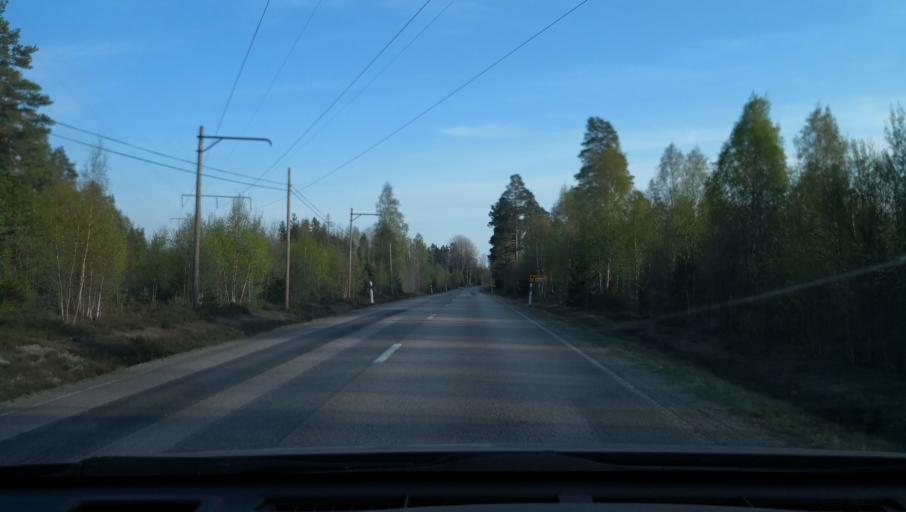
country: SE
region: Uppsala
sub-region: Heby Kommun
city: Heby
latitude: 59.9906
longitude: 16.8315
